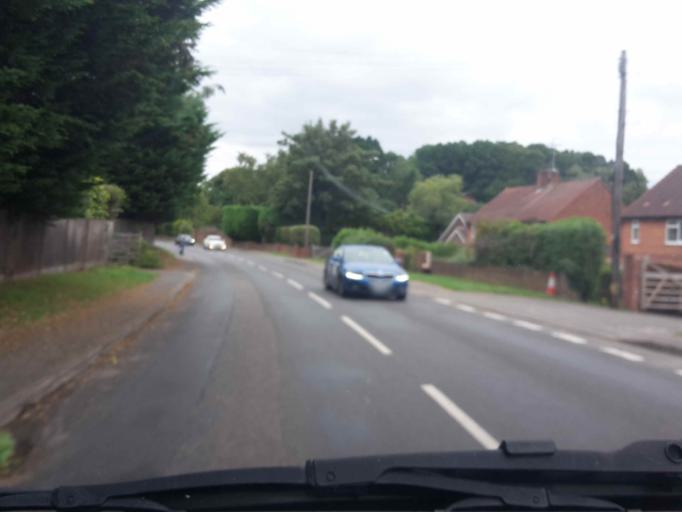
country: GB
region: England
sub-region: Oxfordshire
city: Sonning Common
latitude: 51.5166
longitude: -0.9760
